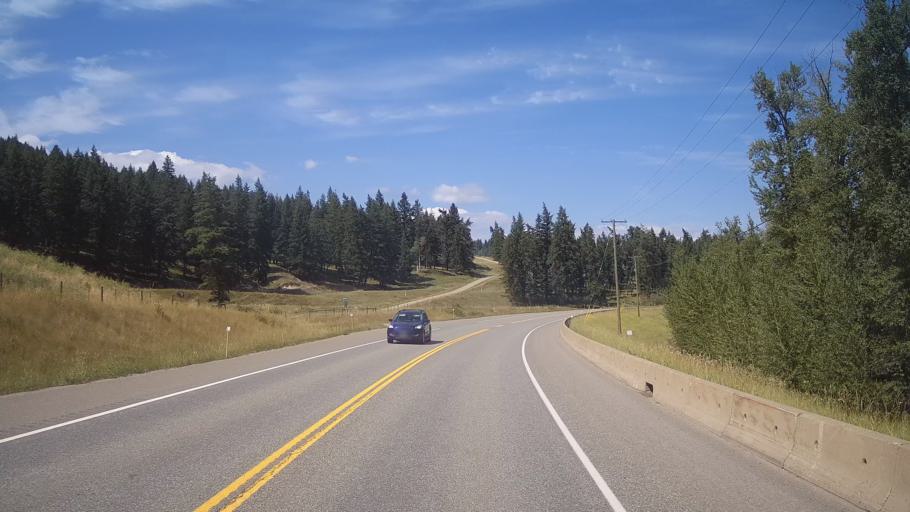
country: CA
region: British Columbia
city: Kamloops
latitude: 51.2597
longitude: -120.1784
